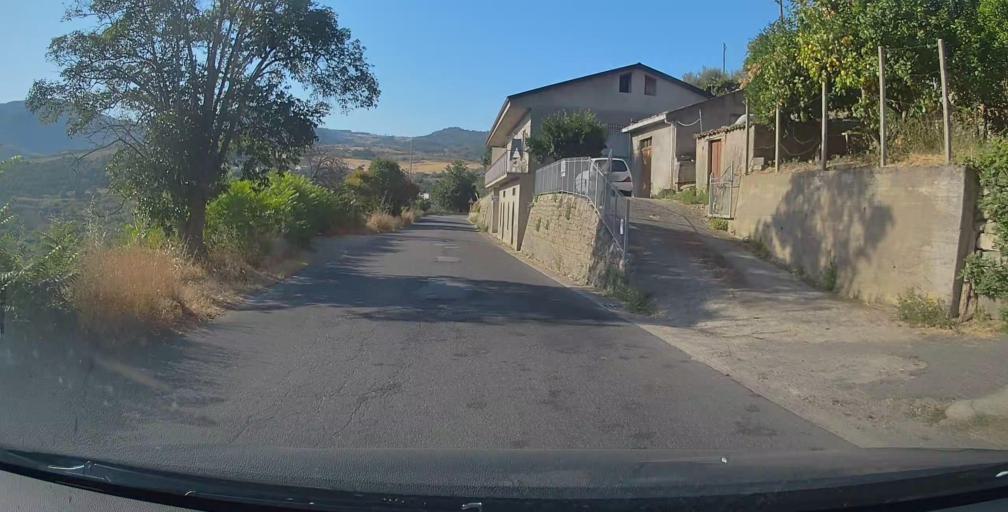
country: IT
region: Sicily
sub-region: Messina
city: Librizzi
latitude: 38.0826
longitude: 14.9741
